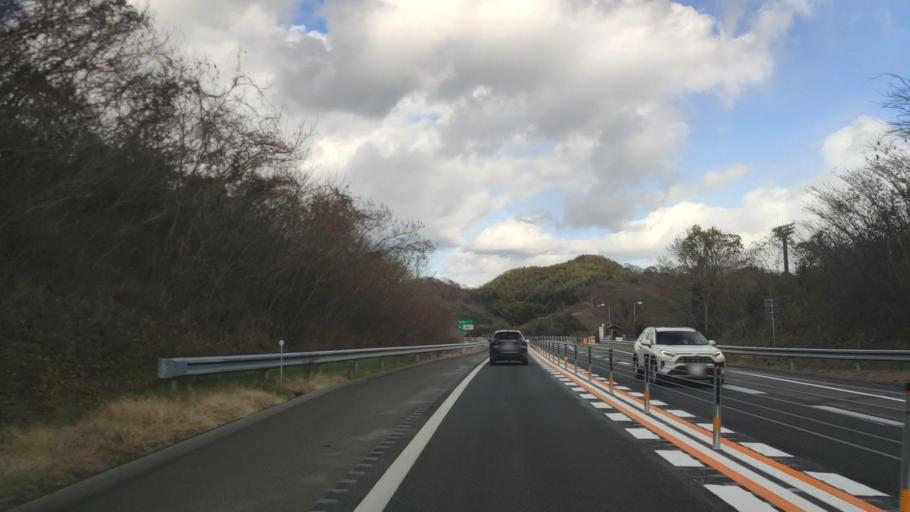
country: JP
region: Hiroshima
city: Innoshima
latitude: 34.3278
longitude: 133.1522
